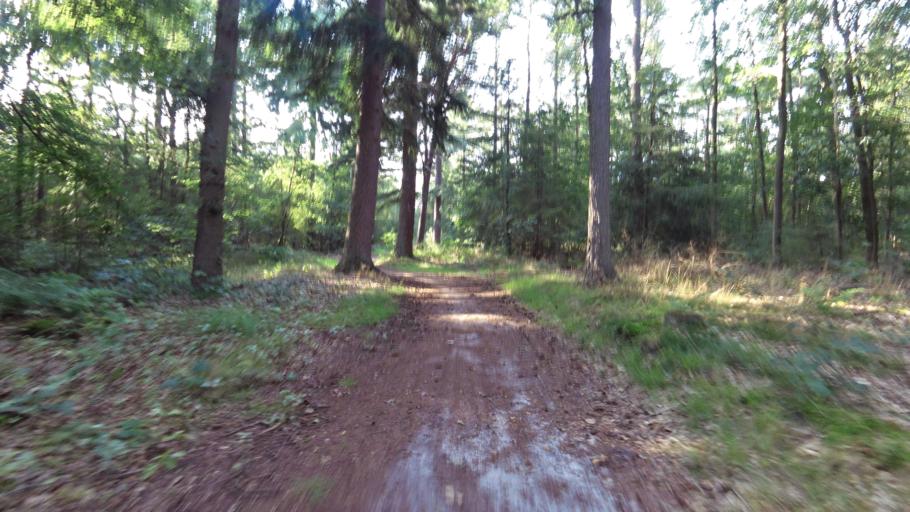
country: NL
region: Utrecht
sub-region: Gemeente Soest
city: Soest
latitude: 52.1554
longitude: 5.2687
